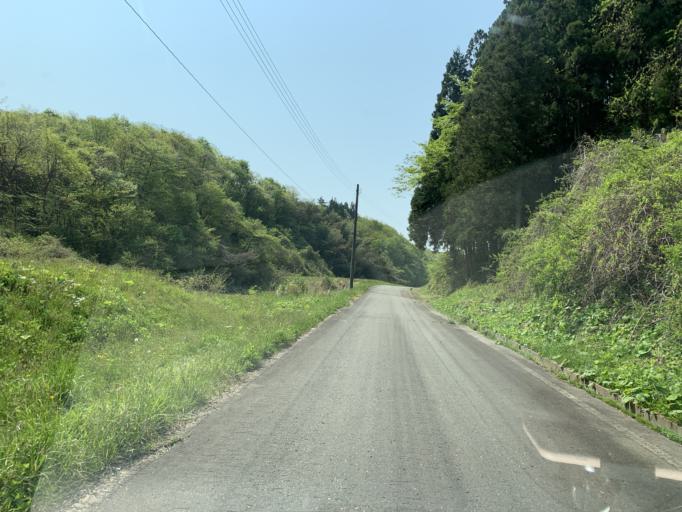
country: JP
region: Iwate
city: Ichinoseki
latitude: 38.8913
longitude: 141.1020
